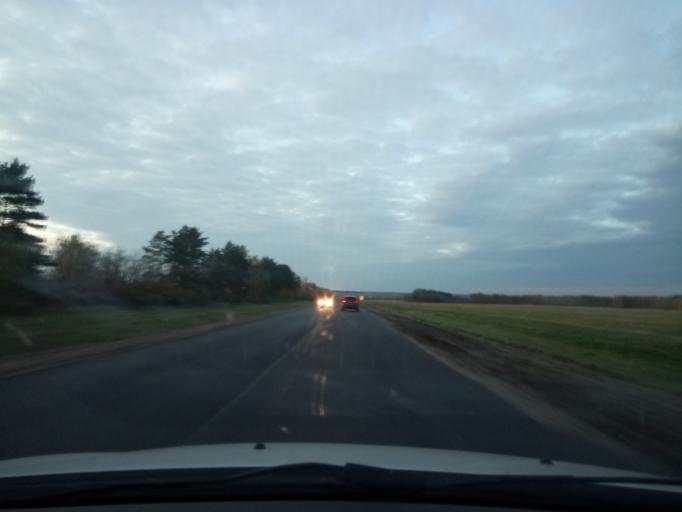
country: RU
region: Nizjnij Novgorod
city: Bol'shoye Murashkino
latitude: 55.8614
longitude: 44.7485
